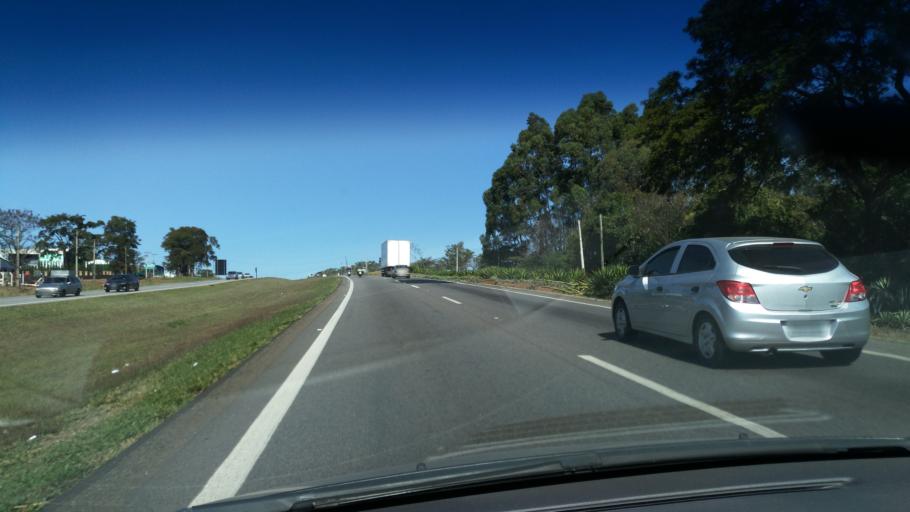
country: BR
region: Sao Paulo
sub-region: Jaguariuna
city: Jaguariuna
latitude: -22.6282
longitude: -47.0067
